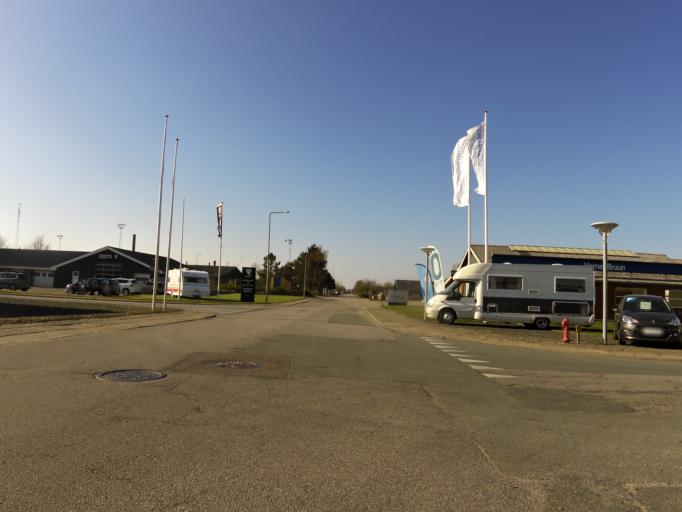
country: DK
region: South Denmark
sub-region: Esbjerg Kommune
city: Ribe
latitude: 55.3506
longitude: 8.7729
